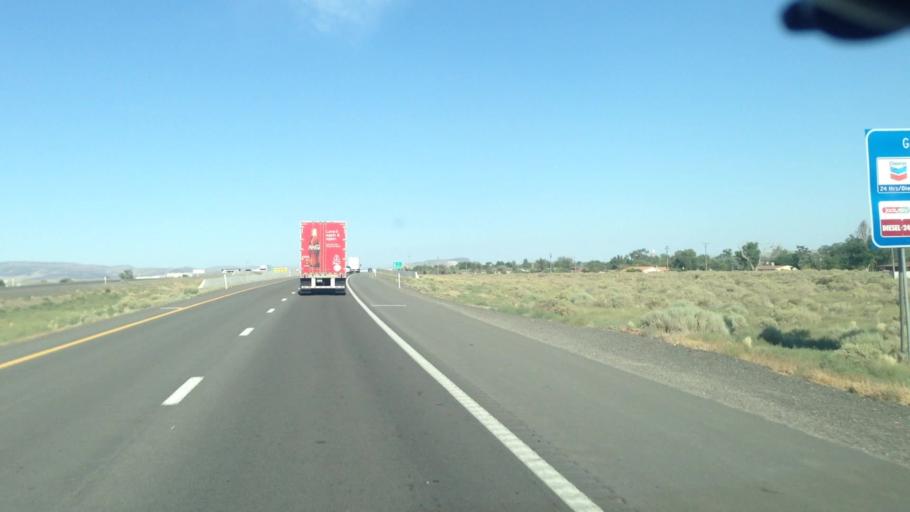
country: US
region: Nevada
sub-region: Lyon County
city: Fernley
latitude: 39.6149
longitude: -119.2402
